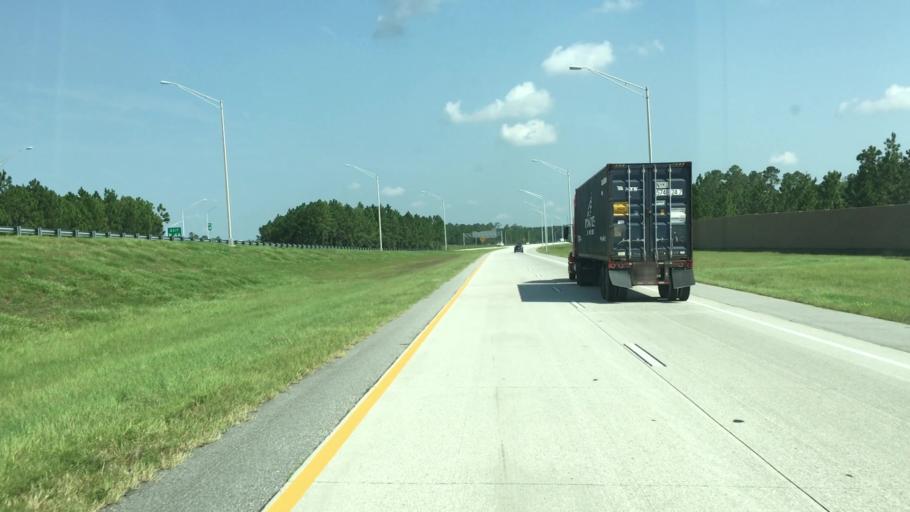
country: US
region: Florida
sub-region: Saint Johns County
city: Fruit Cove
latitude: 30.1161
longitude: -81.5130
